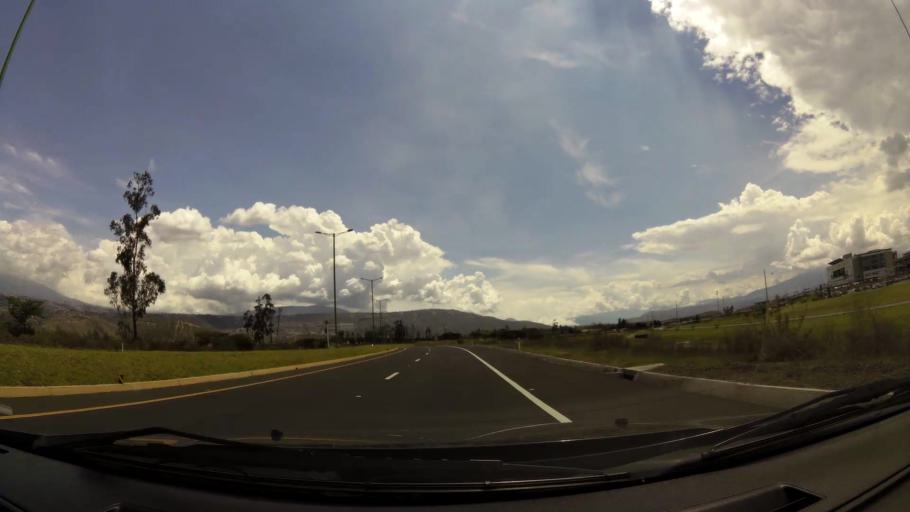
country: EC
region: Pichincha
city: Quito
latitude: -0.1279
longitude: -78.3628
